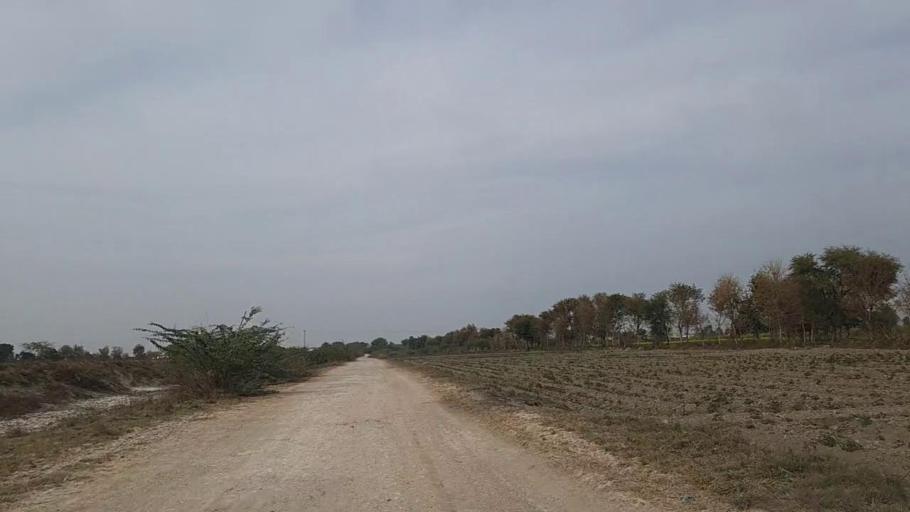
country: PK
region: Sindh
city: Daur
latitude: 26.4216
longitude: 68.4195
